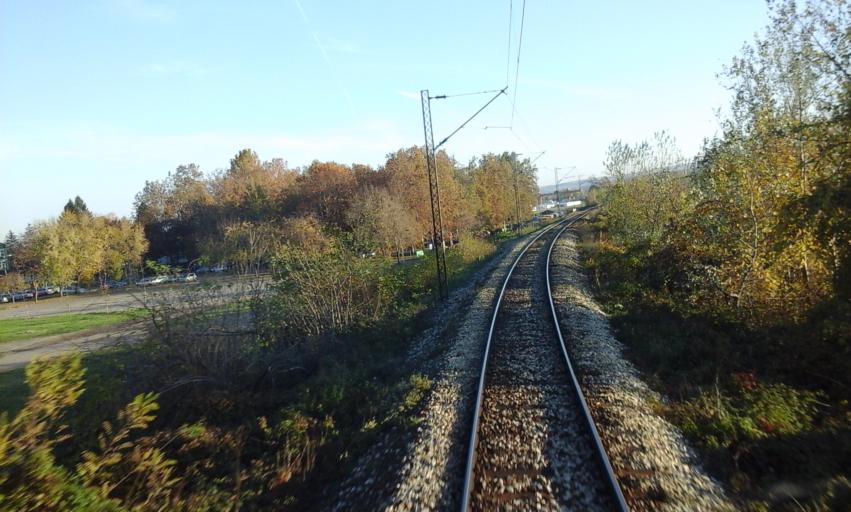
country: RS
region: Autonomna Pokrajina Vojvodina
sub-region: Juznobacki Okrug
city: Petrovaradin
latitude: 45.2545
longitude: 19.8789
